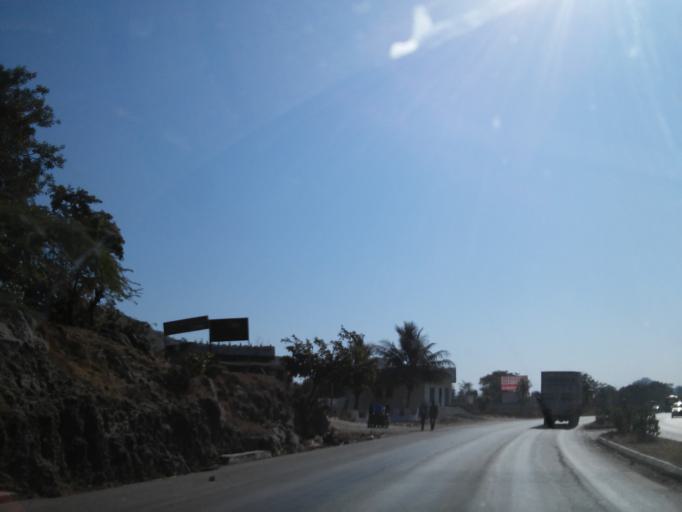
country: IN
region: Rajasthan
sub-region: Dungarpur
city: Dungarpur
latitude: 24.1433
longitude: 73.6917
